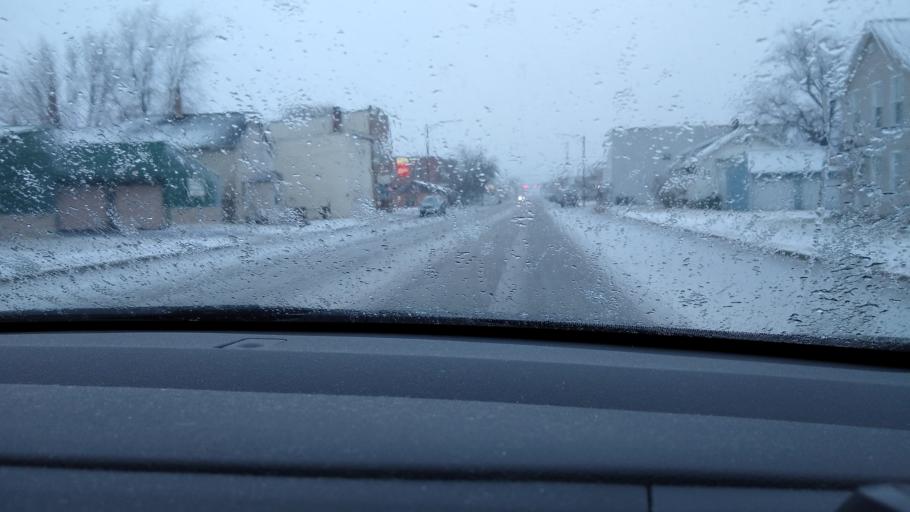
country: US
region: Michigan
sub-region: Delta County
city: Escanaba
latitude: 45.7428
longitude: -87.0612
